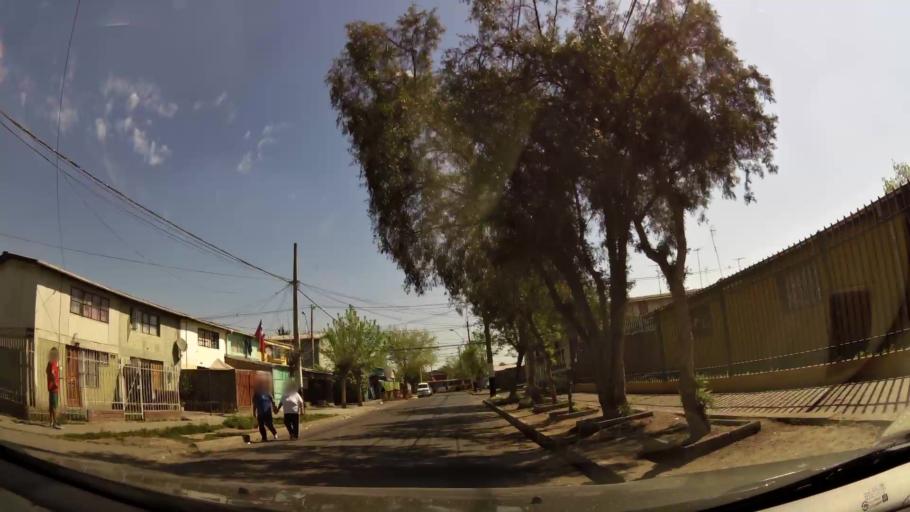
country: CL
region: Santiago Metropolitan
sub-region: Provincia de Cordillera
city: Puente Alto
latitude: -33.6228
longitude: -70.6067
